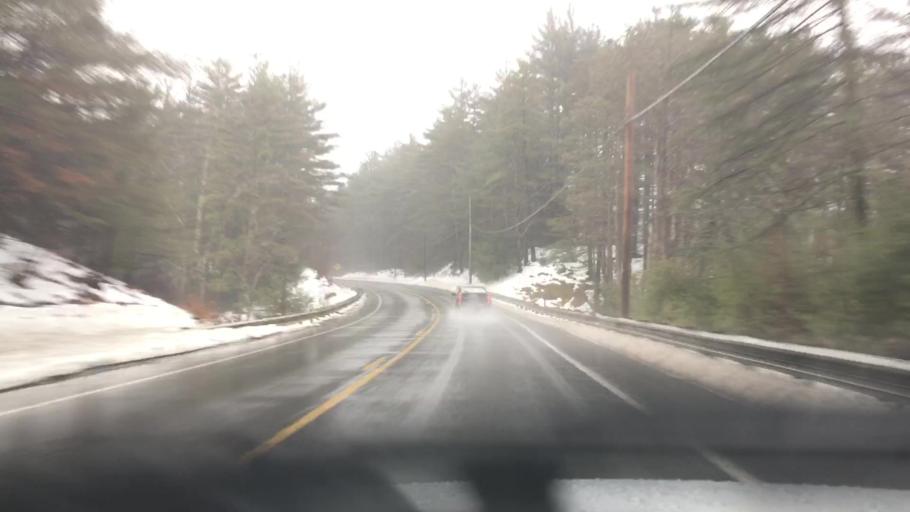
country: US
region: Massachusetts
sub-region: Franklin County
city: Orange
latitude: 42.5361
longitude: -72.3096
